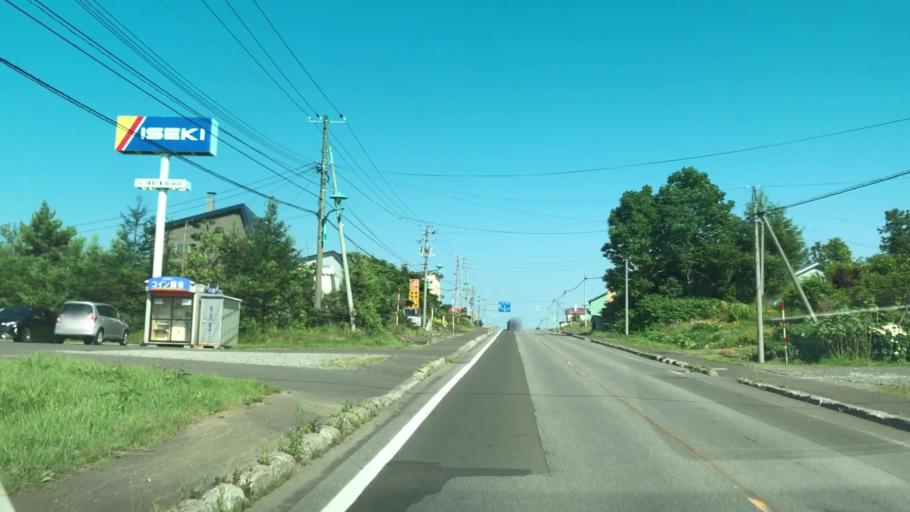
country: JP
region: Hokkaido
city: Iwanai
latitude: 42.9822
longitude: 140.5698
